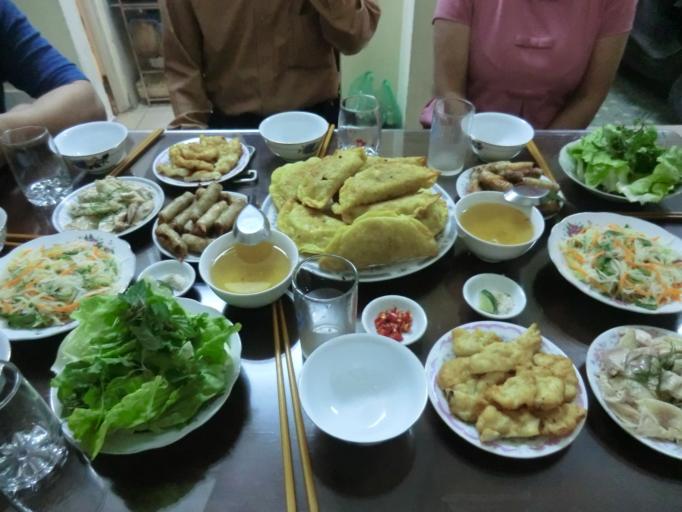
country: VN
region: Ha Noi
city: Hoan Kiem
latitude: 21.0471
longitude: 105.8568
